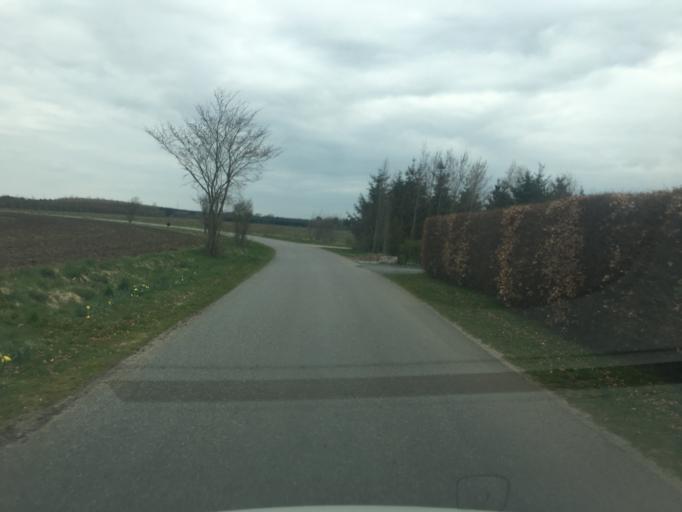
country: DK
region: South Denmark
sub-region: Aabenraa Kommune
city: Tinglev
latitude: 55.0437
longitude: 9.1469
